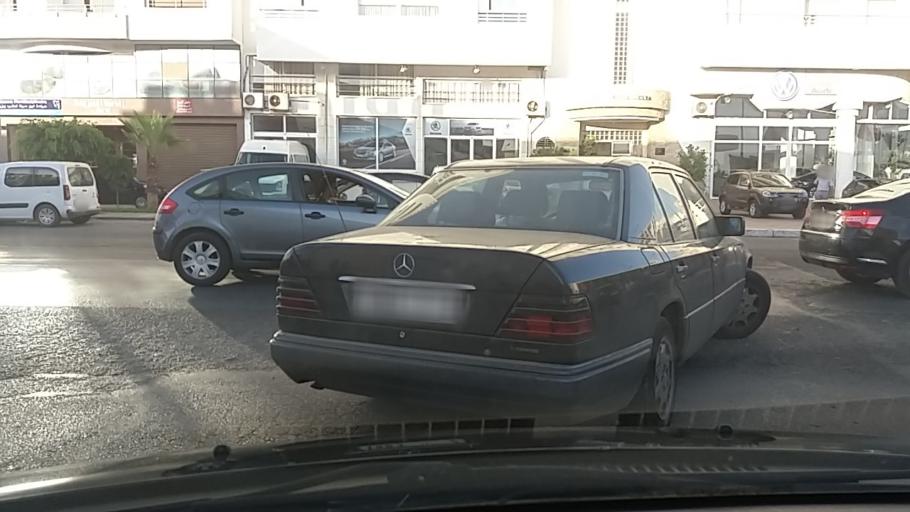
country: MA
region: Gharb-Chrarda-Beni Hssen
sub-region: Kenitra Province
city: Kenitra
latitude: 34.2559
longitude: -6.5972
